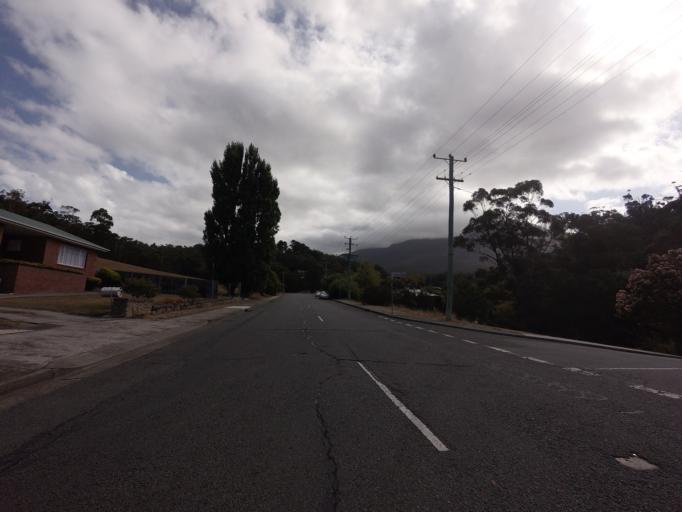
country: AU
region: Tasmania
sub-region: Hobart
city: Dynnyrne
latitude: -42.8974
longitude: 147.2912
